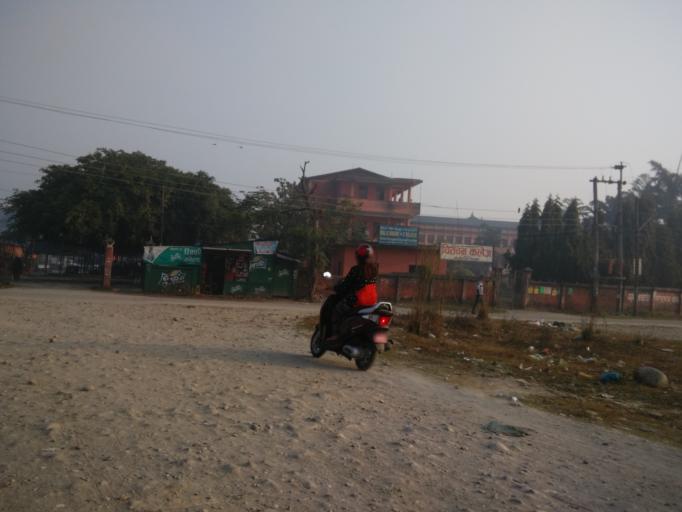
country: NP
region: Central Region
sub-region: Narayani Zone
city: Bharatpur
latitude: 27.6966
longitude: 84.4259
